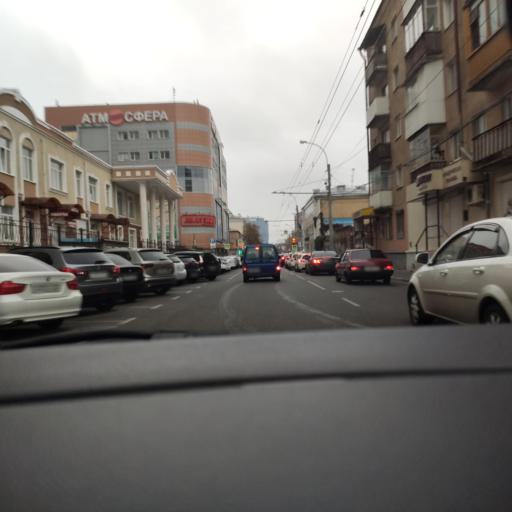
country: RU
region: Voronezj
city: Voronezh
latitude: 51.6626
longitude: 39.1933
